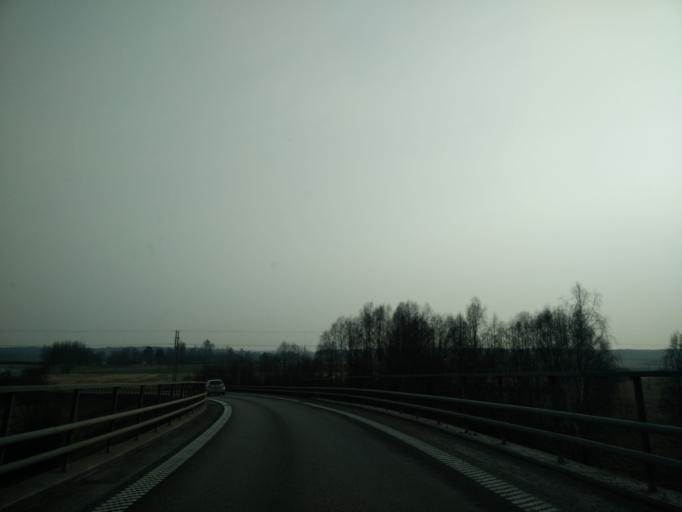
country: SE
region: Vaermland
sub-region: Karlstads Kommun
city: Karlstad
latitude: 59.4268
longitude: 13.4080
